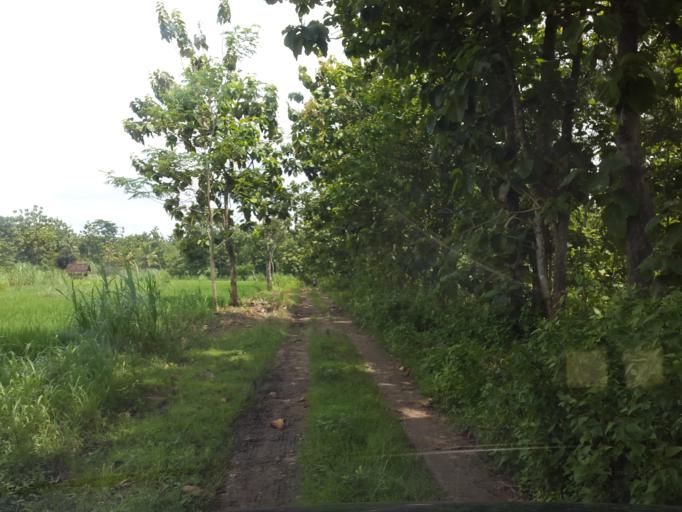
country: ID
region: Daerah Istimewa Yogyakarta
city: Wonosari
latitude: -7.9502
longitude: 110.6572
